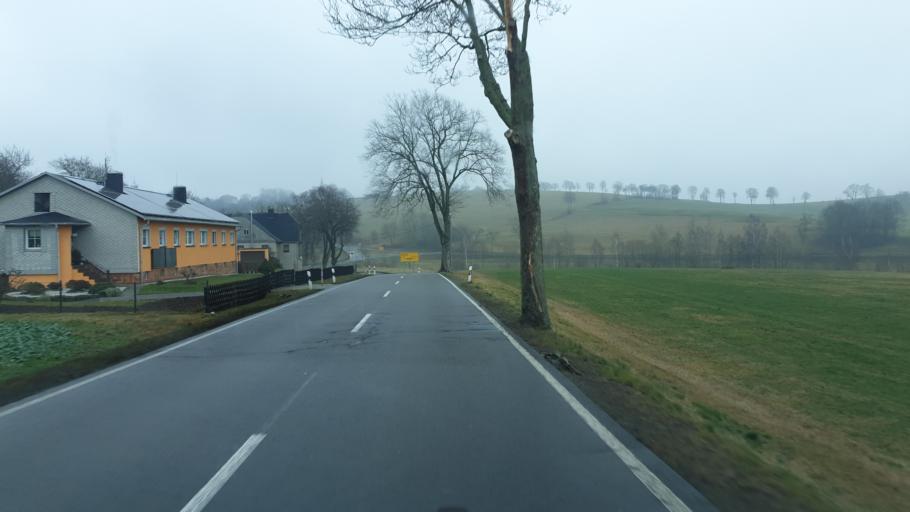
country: DE
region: Saxony
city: Sayda
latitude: 50.7176
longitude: 13.4051
